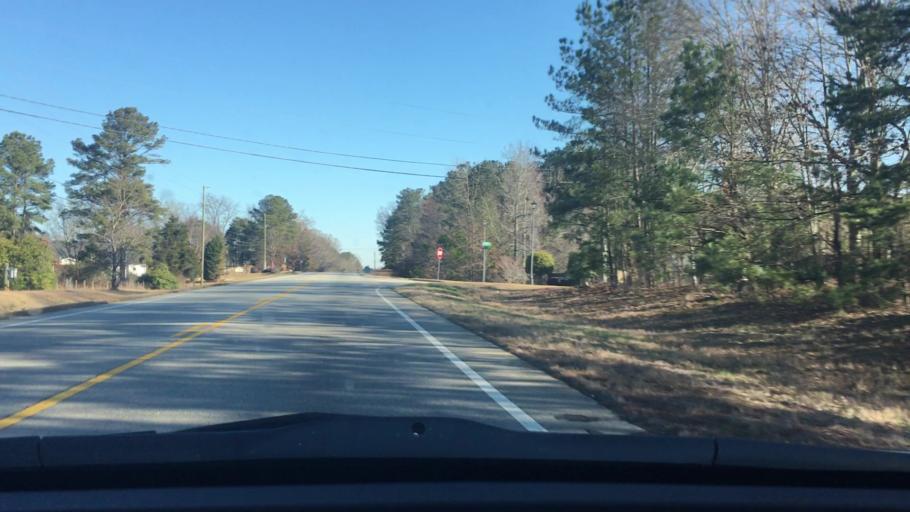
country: US
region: Georgia
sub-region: Henry County
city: McDonough
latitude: 33.4936
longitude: -84.0845
